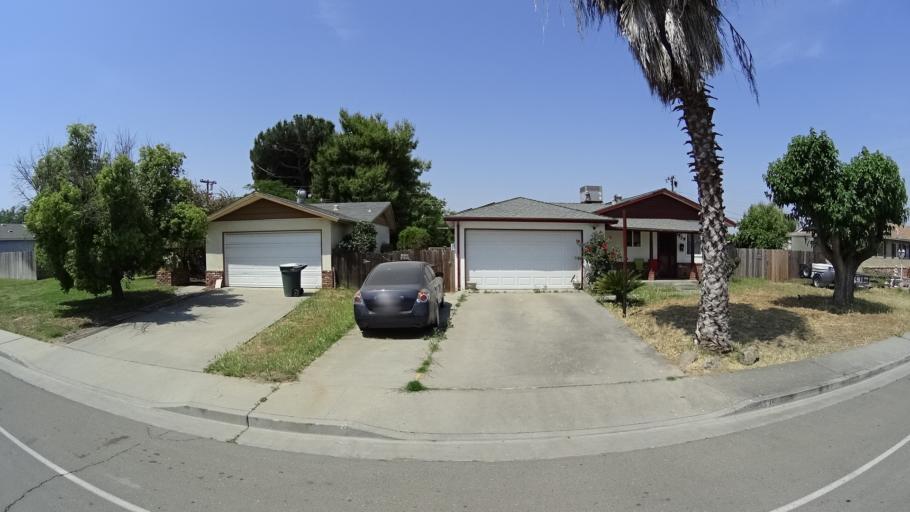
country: US
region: California
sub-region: Kings County
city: Lemoore
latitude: 36.3198
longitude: -119.7809
